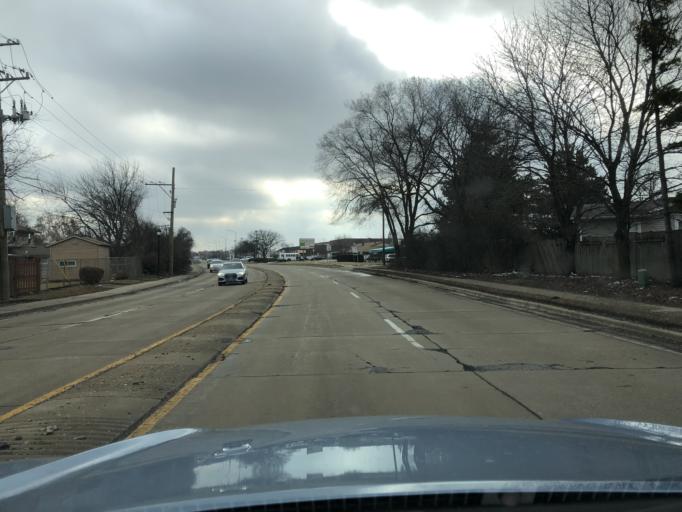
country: US
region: Illinois
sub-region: DuPage County
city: Itasca
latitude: 42.0078
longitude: -88.0038
